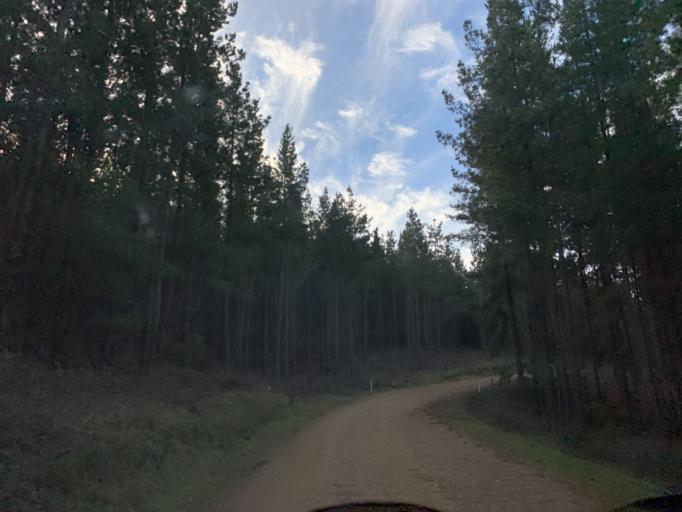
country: AU
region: Victoria
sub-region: Mansfield
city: Mansfield
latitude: -36.8942
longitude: 146.1187
